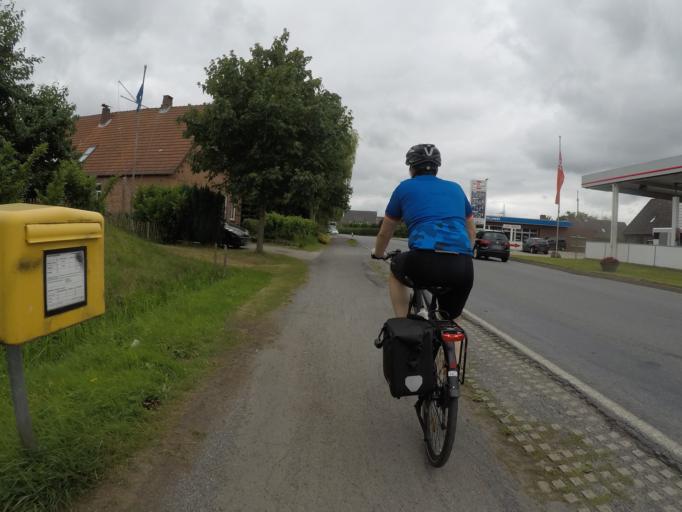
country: DE
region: Schleswig-Holstein
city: Haseldorf
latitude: 53.5907
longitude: 9.5682
